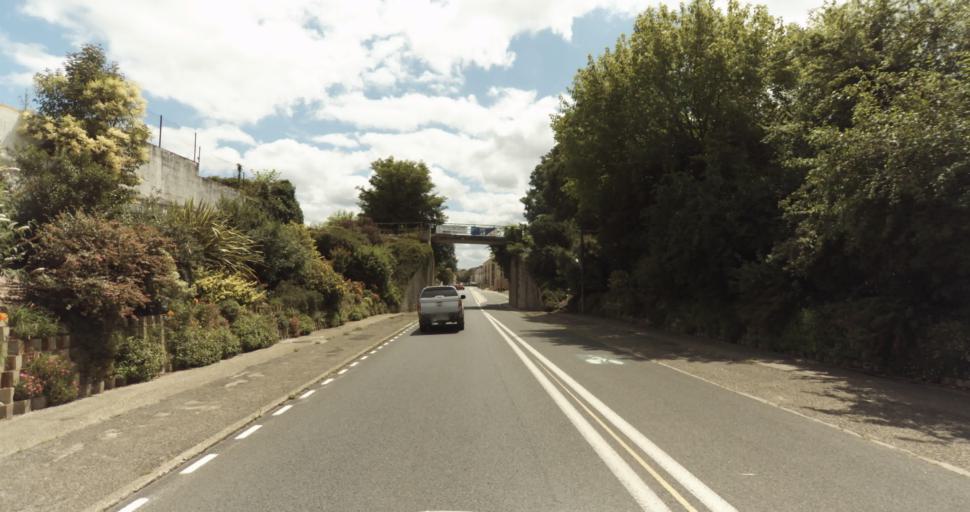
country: FR
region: Aquitaine
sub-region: Departement de la Gironde
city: Bazas
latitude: 44.4333
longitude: -0.2189
